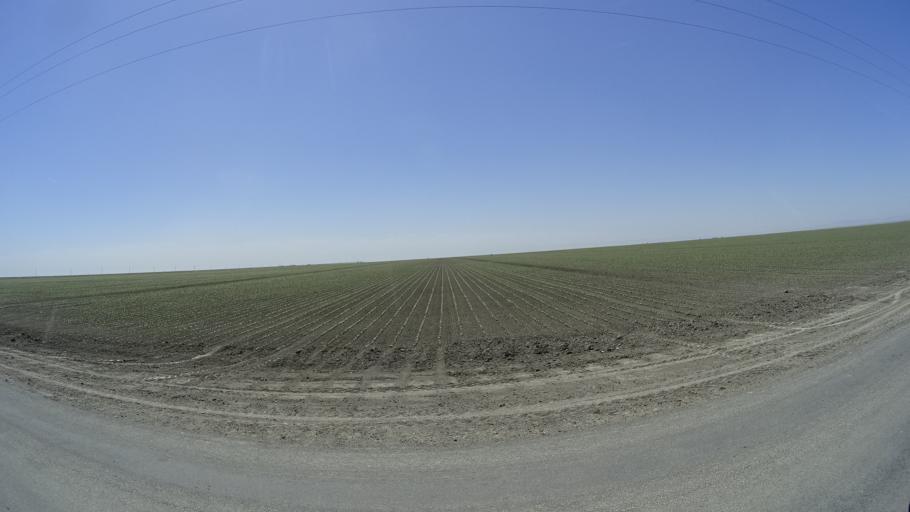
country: US
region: California
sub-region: Kings County
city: Corcoran
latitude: 36.0214
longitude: -119.6492
